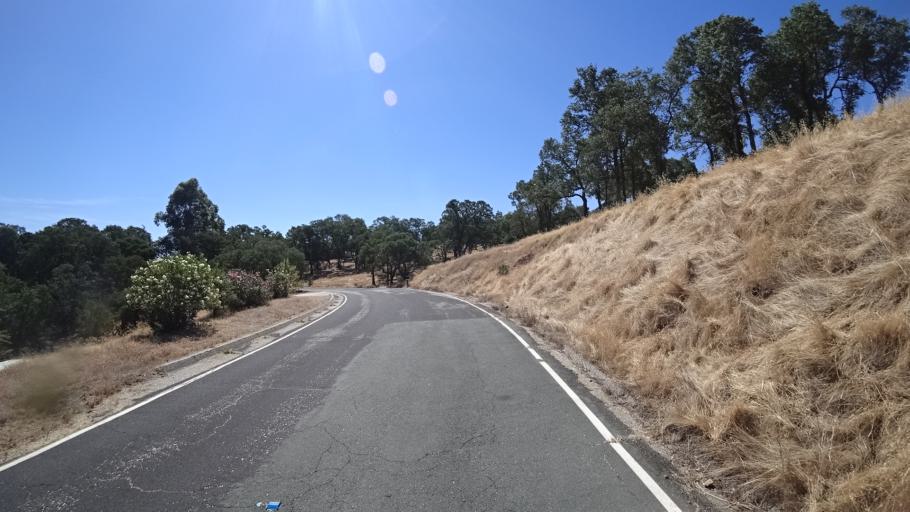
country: US
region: California
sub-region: Calaveras County
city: Rancho Calaveras
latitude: 38.1556
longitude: -120.8425
